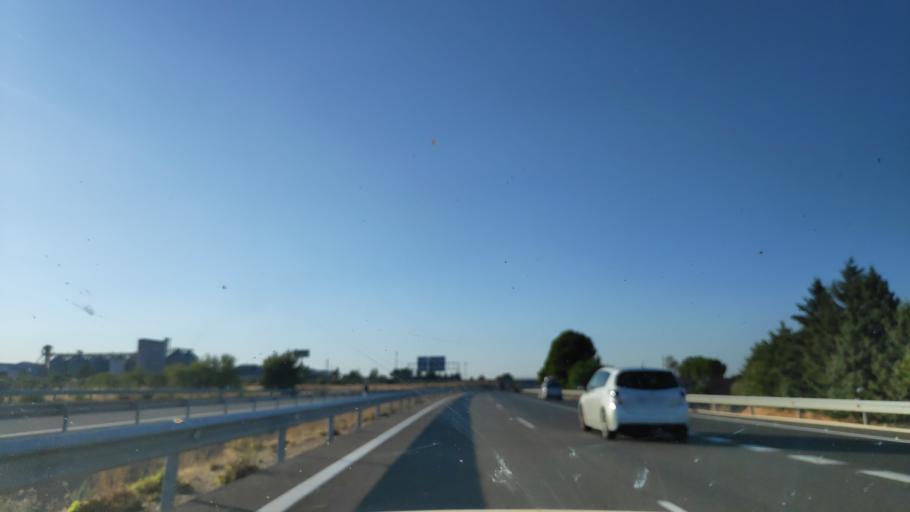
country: ES
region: Castille-La Mancha
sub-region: Provincia de Cuenca
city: Tarancon
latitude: 40.0066
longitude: -3.0281
